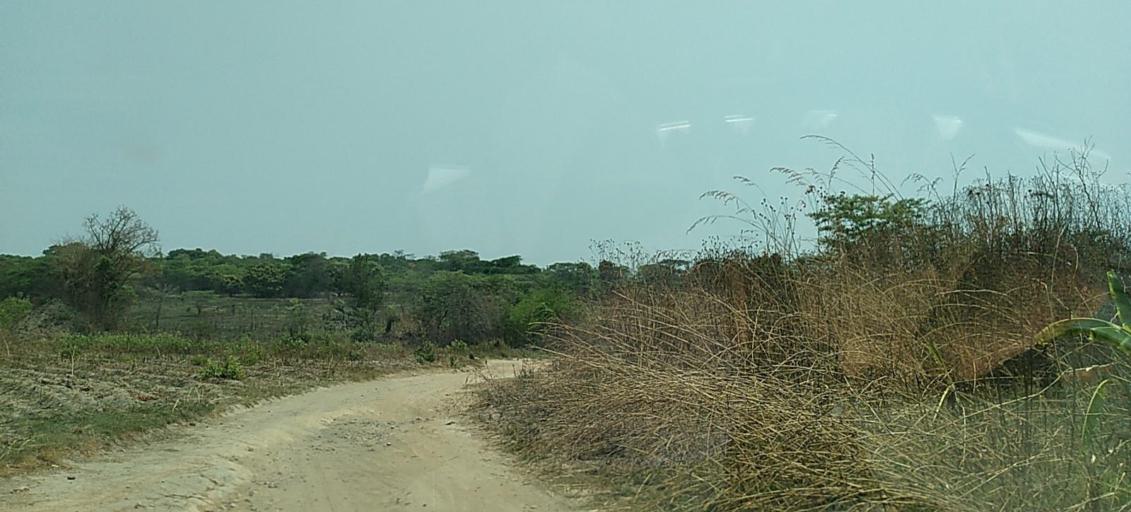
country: ZM
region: Copperbelt
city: Kalulushi
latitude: -12.9566
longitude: 28.1485
